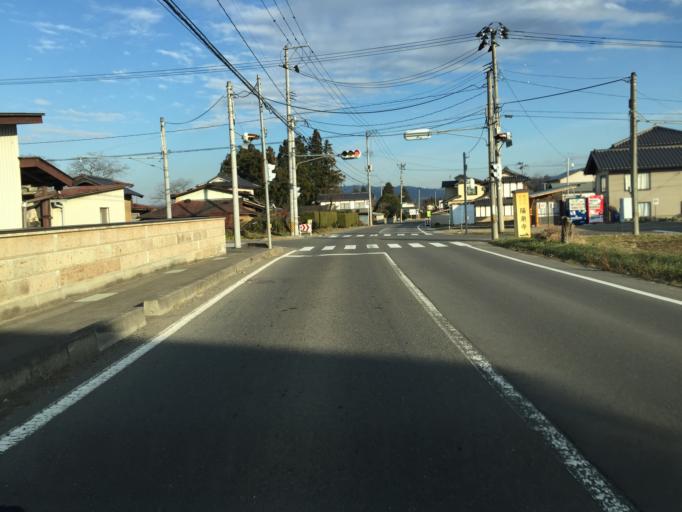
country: JP
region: Fukushima
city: Fukushima-shi
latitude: 37.7290
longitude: 140.4174
